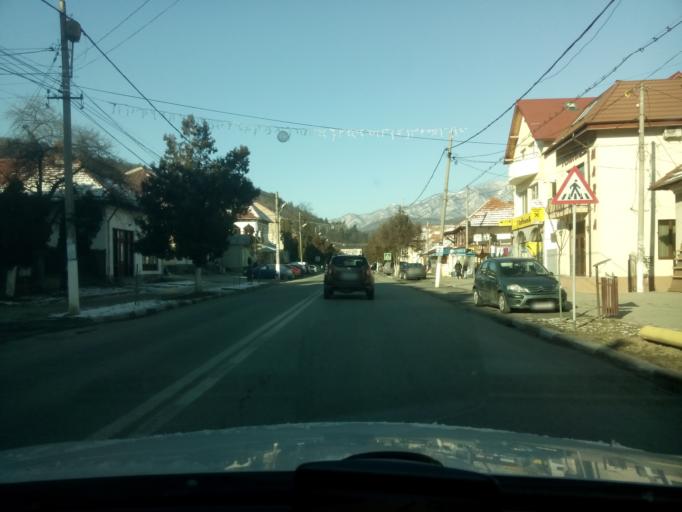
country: RO
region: Valcea
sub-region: Oras Calimanesti
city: Calimanesti
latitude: 45.2410
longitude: 24.3410
